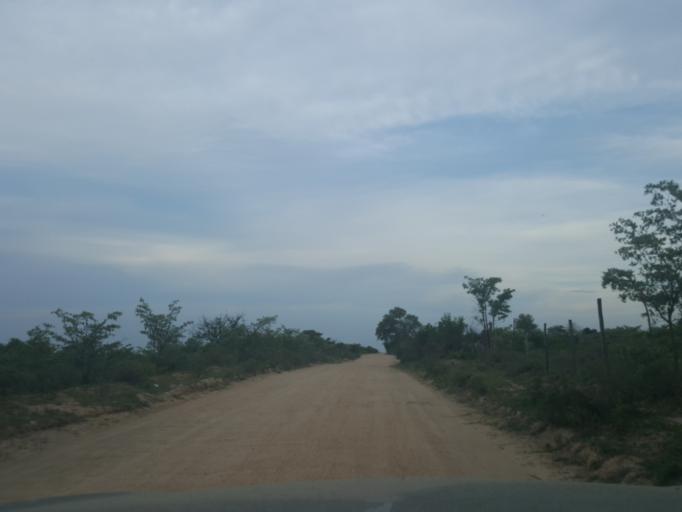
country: ZA
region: Limpopo
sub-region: Mopani District Municipality
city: Hoedspruit
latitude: -24.5853
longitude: 30.9774
